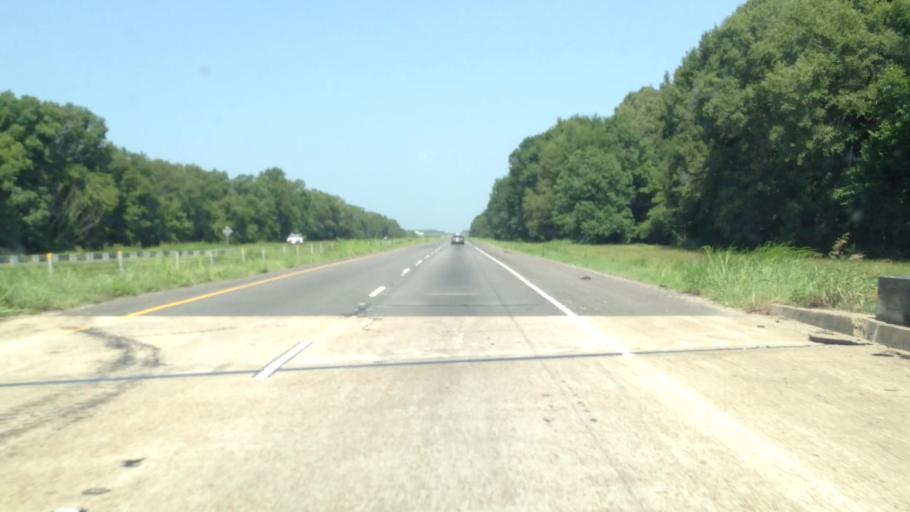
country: US
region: Louisiana
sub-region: Richland Parish
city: Delhi
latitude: 32.4352
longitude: -91.4432
